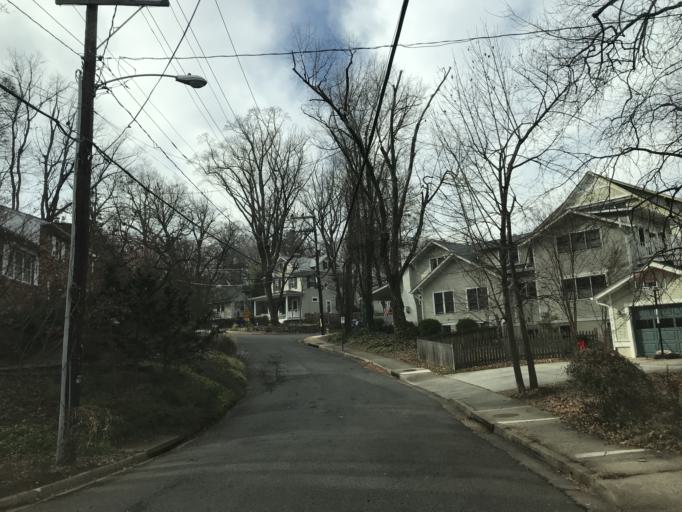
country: US
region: Virginia
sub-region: Arlington County
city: Arlington
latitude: 38.8989
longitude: -77.0963
